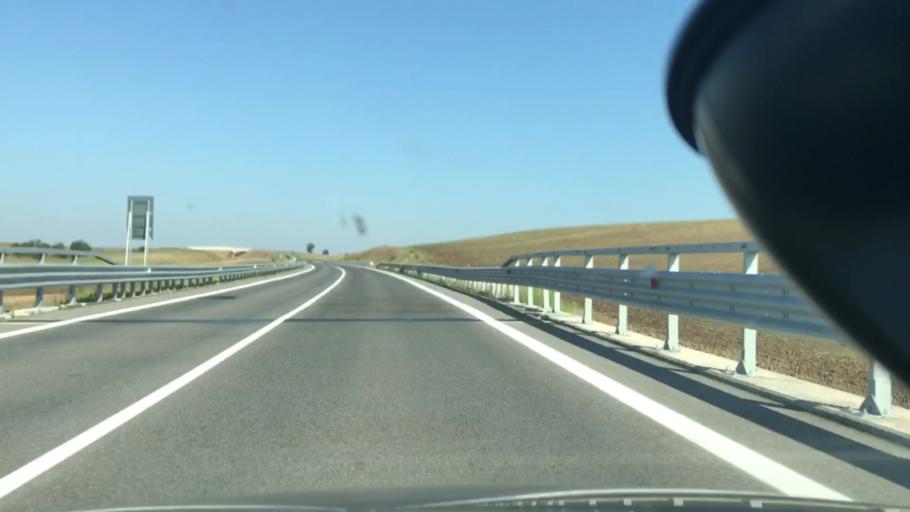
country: IT
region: Basilicate
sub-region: Provincia di Potenza
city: Palazzo San Gervasio
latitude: 40.9637
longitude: 16.0106
